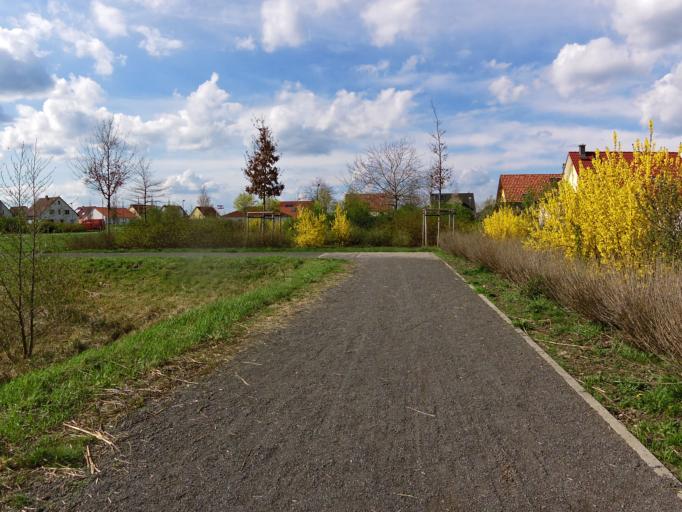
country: DE
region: Saxony
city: Markranstadt
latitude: 51.3253
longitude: 12.2800
